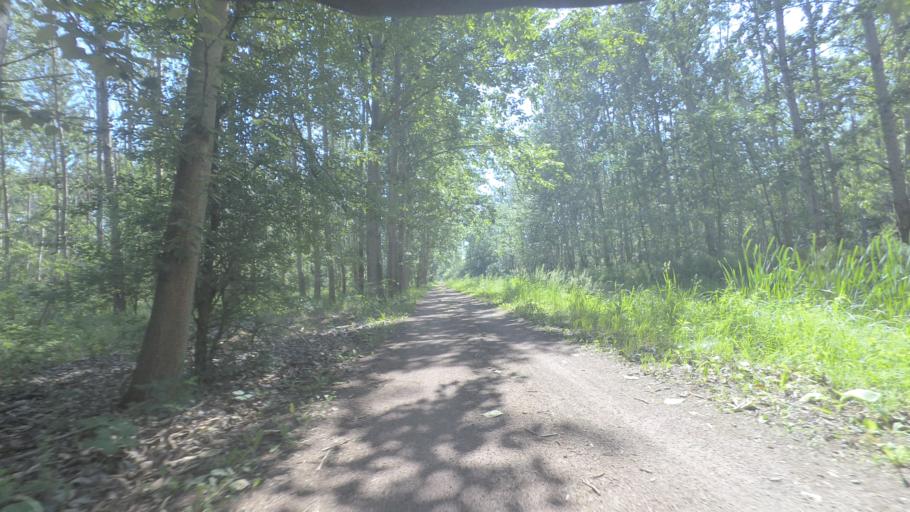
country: DE
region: Saxony-Anhalt
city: Vockerode
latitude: 51.8264
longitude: 12.3465
